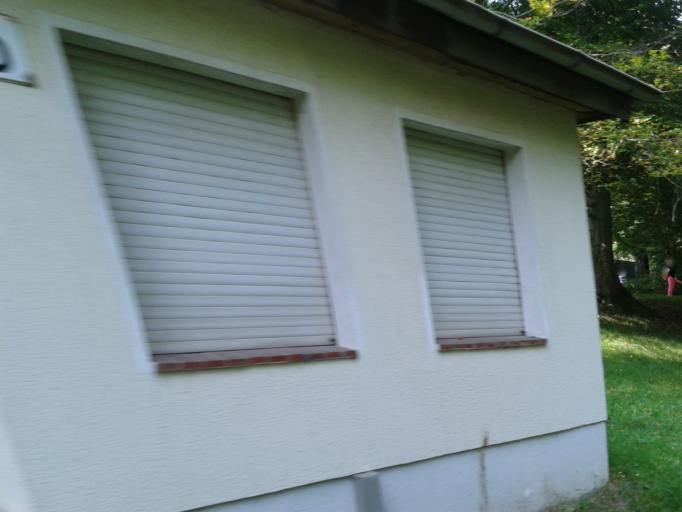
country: DE
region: Saxony
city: Dresden
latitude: 51.0379
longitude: 13.7562
